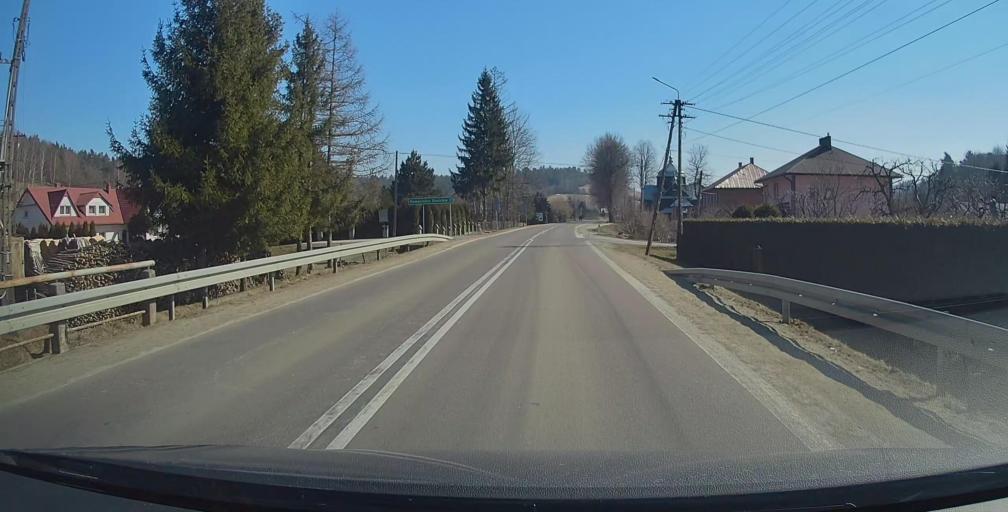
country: PL
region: Subcarpathian Voivodeship
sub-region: Powiat przemyski
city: Bircza
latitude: 49.5728
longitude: 22.5524
